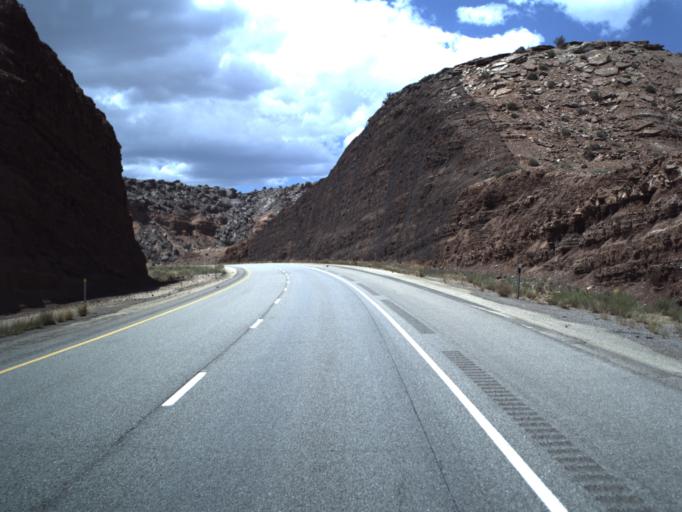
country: US
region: Utah
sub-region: Emery County
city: Ferron
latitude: 38.8320
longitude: -111.1306
